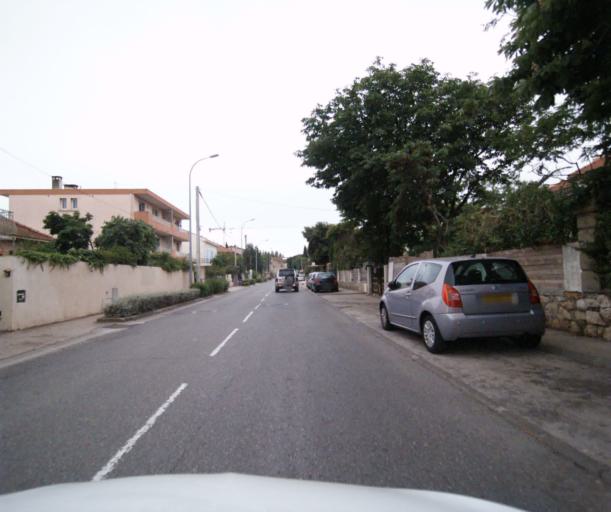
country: FR
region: Provence-Alpes-Cote d'Azur
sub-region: Departement du Var
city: La Seyne-sur-Mer
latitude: 43.0812
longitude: 5.8910
